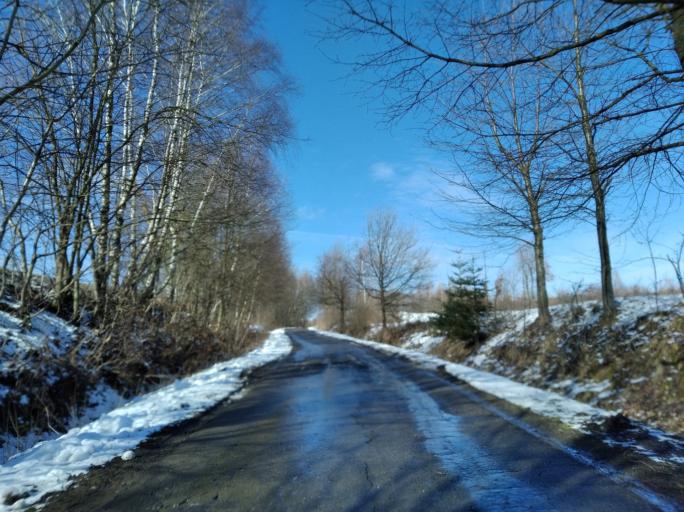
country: PL
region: Subcarpathian Voivodeship
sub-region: Powiat brzozowski
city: Jablonica Polska
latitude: 49.7268
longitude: 21.8750
